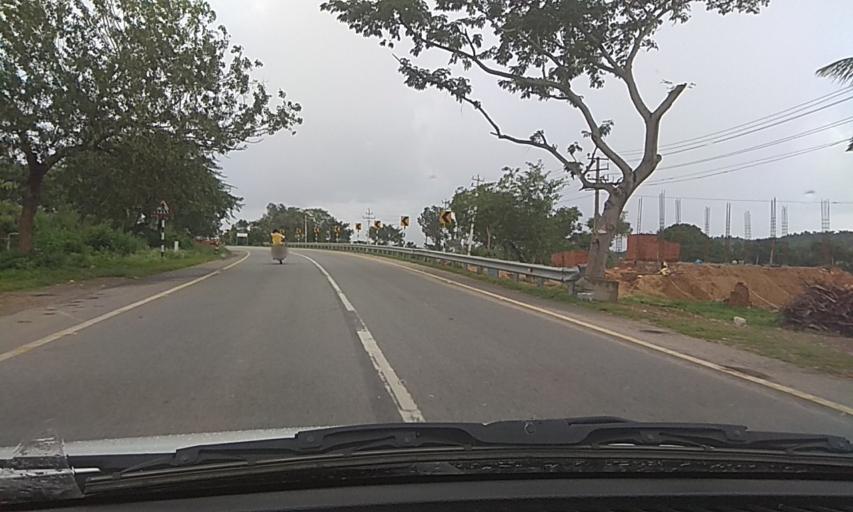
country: IN
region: Karnataka
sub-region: Mandya
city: Maddur
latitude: 12.7884
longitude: 77.0480
